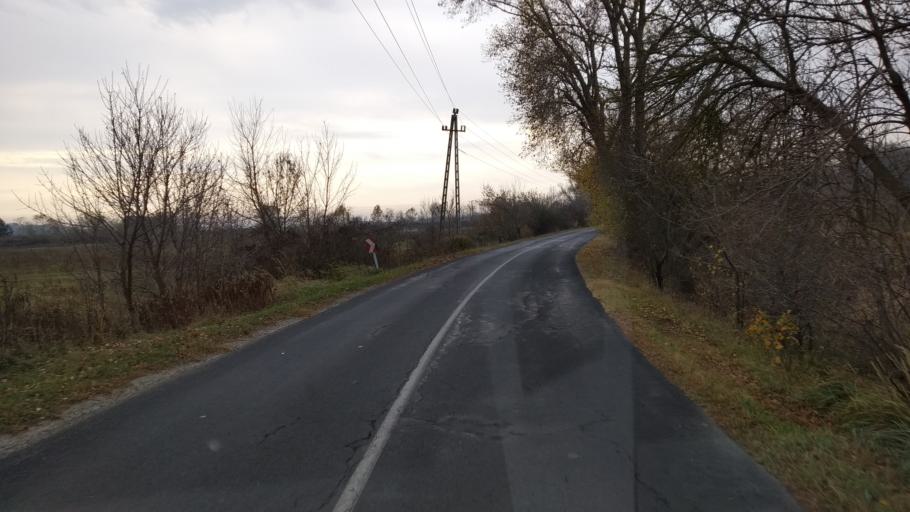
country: HU
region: Pest
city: Tahitotfalu
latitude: 47.7822
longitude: 19.0932
